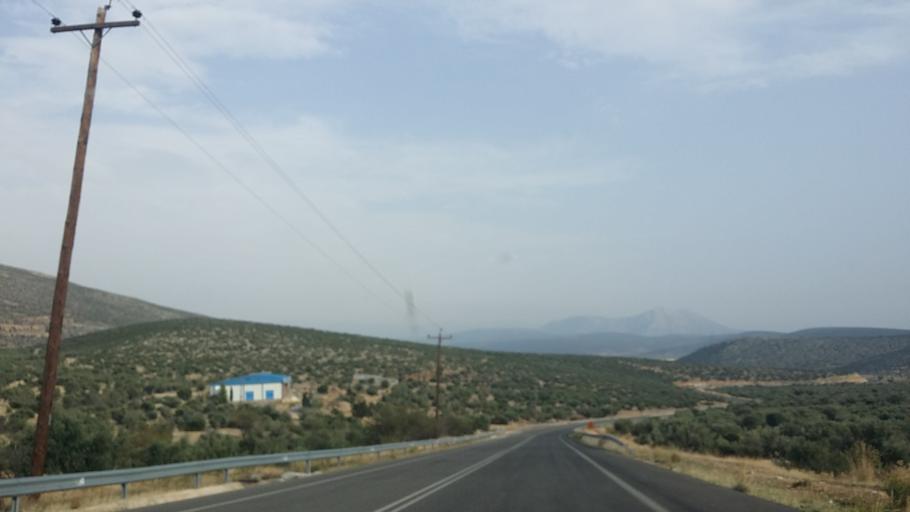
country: GR
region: Central Greece
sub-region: Nomos Voiotias
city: Korini
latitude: 38.2556
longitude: 22.9189
